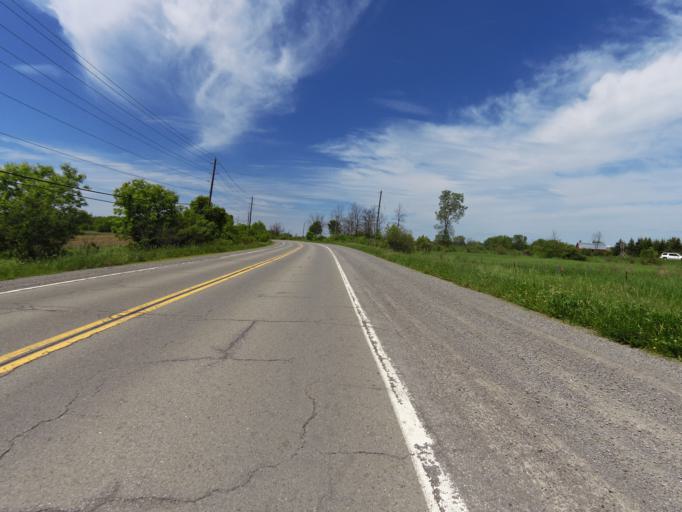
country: CA
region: Ontario
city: Ottawa
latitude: 45.3732
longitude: -75.5698
